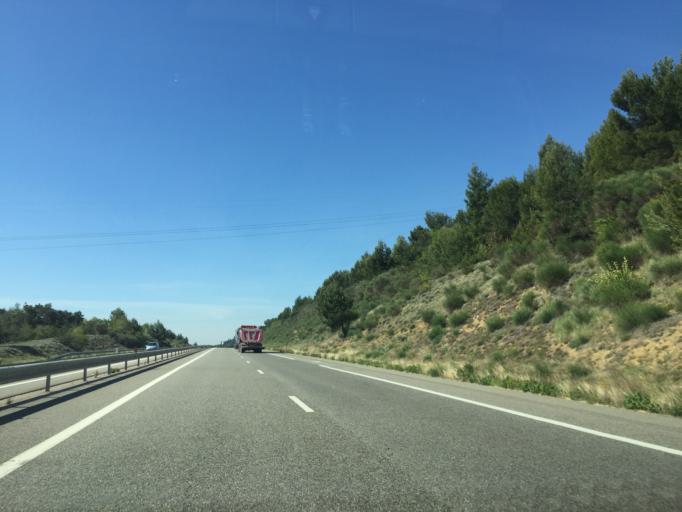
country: FR
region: Provence-Alpes-Cote d'Azur
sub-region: Departement des Alpes-de-Haute-Provence
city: Volonne
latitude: 44.0835
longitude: 5.9846
